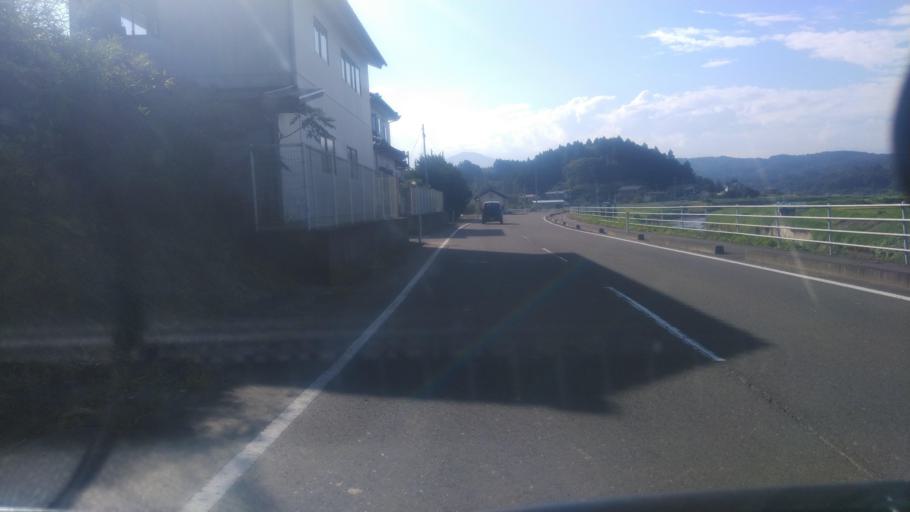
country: JP
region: Miyagi
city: Okawara
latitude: 38.0804
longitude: 140.7300
